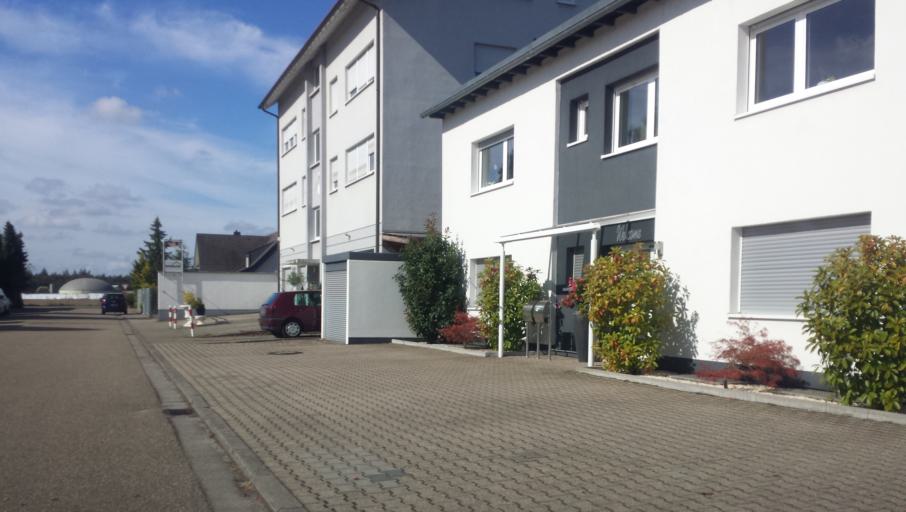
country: DE
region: Baden-Wuerttemberg
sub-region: Karlsruhe Region
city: Waghausel
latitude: 49.2498
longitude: 8.5374
